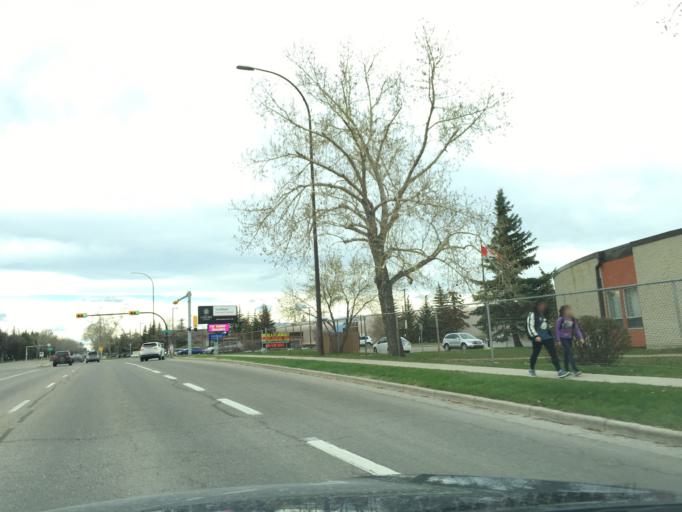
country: CA
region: Alberta
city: Calgary
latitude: 50.9615
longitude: -114.1053
